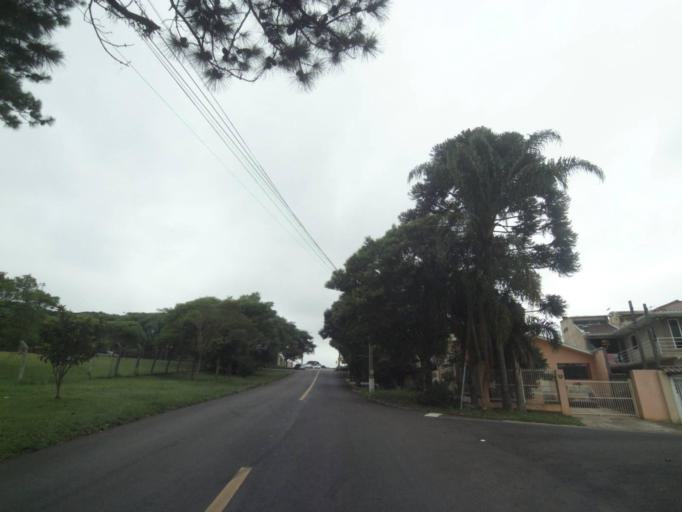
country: BR
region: Parana
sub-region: Curitiba
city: Curitiba
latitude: -25.4906
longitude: -49.3537
